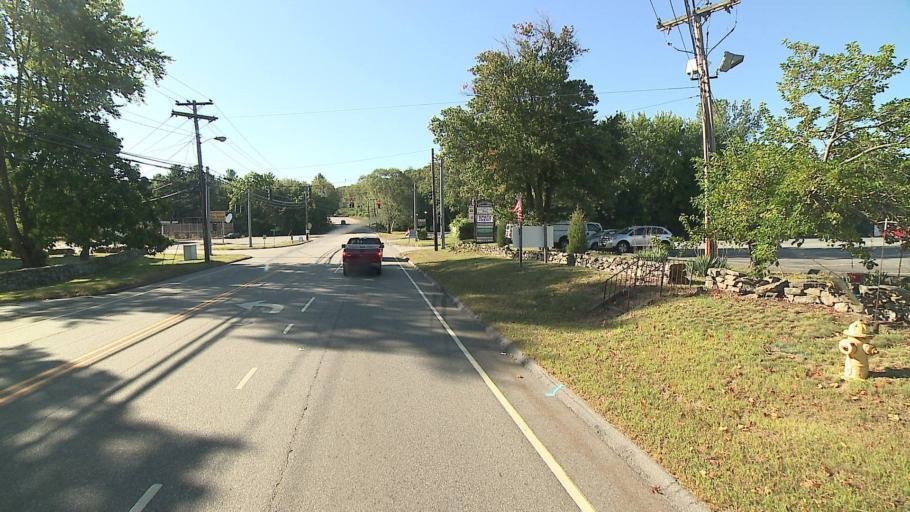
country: US
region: Connecticut
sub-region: New London County
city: Gales Ferry
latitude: 41.4268
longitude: -72.0819
